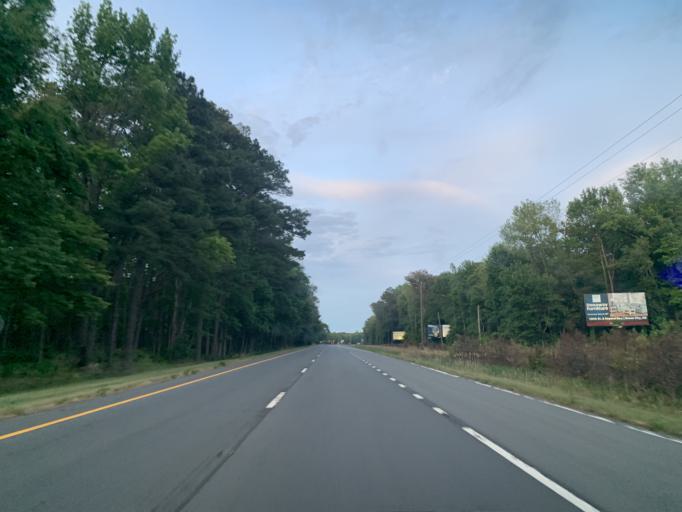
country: US
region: Maryland
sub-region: Wicomico County
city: Pittsville
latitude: 38.3847
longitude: -75.3199
